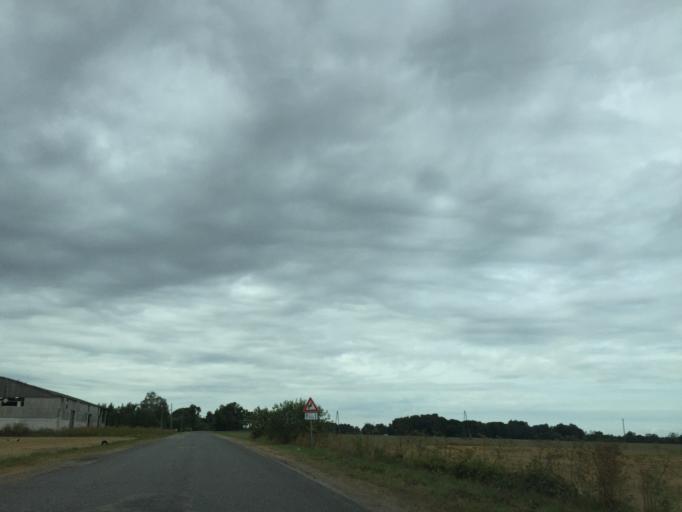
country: LV
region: Engure
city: Smarde
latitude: 56.8075
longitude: 23.3264
